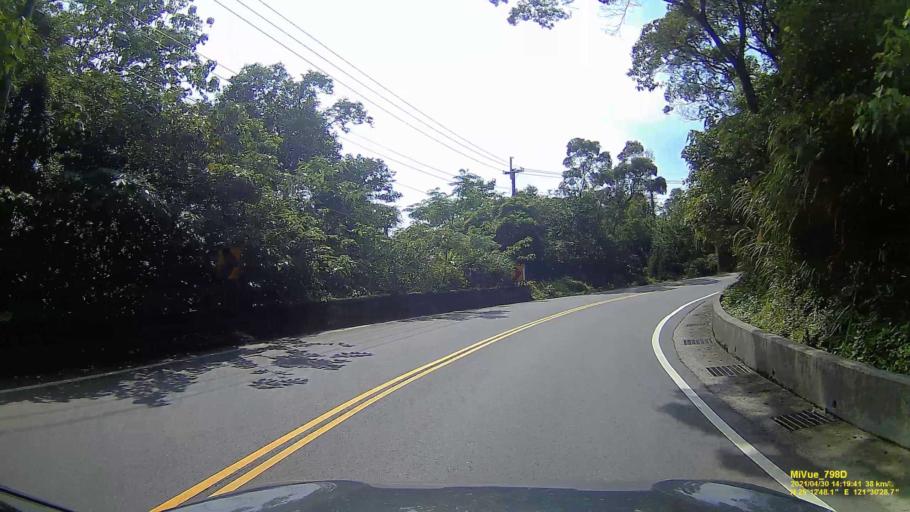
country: TW
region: Taipei
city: Taipei
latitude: 25.2134
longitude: 121.5078
